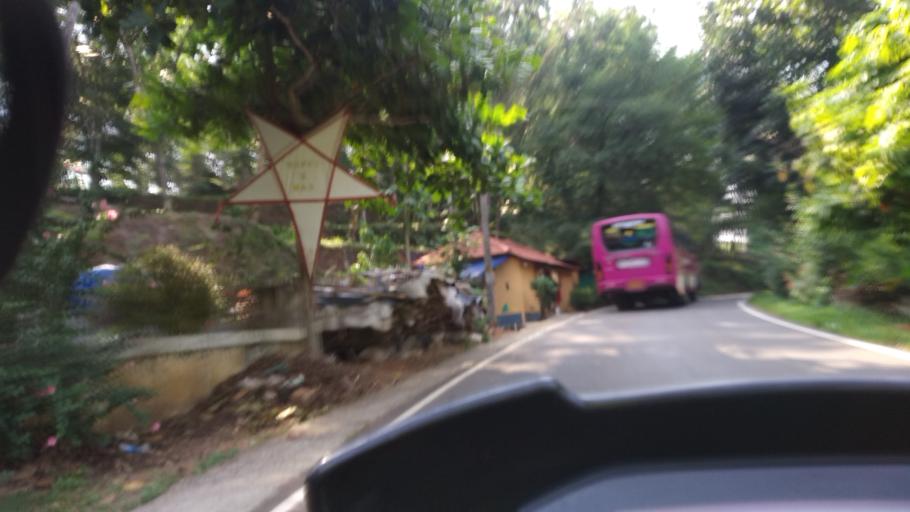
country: IN
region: Kerala
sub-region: Ernakulam
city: Piravam
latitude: 9.8173
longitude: 76.5570
